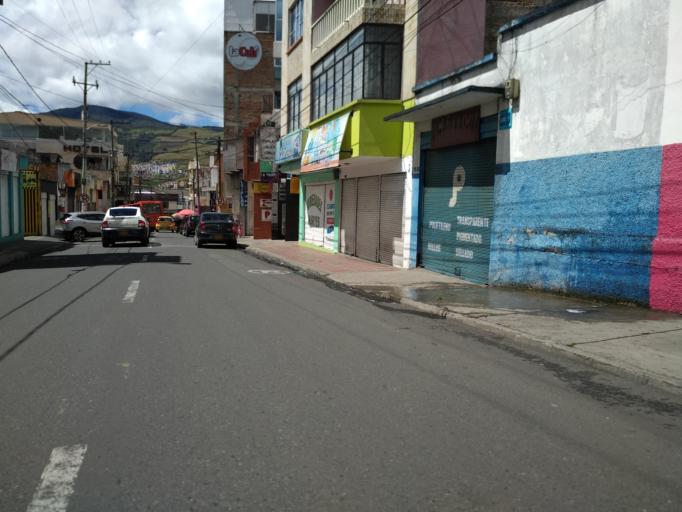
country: CO
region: Narino
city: Pasto
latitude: 1.2099
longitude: -77.2790
